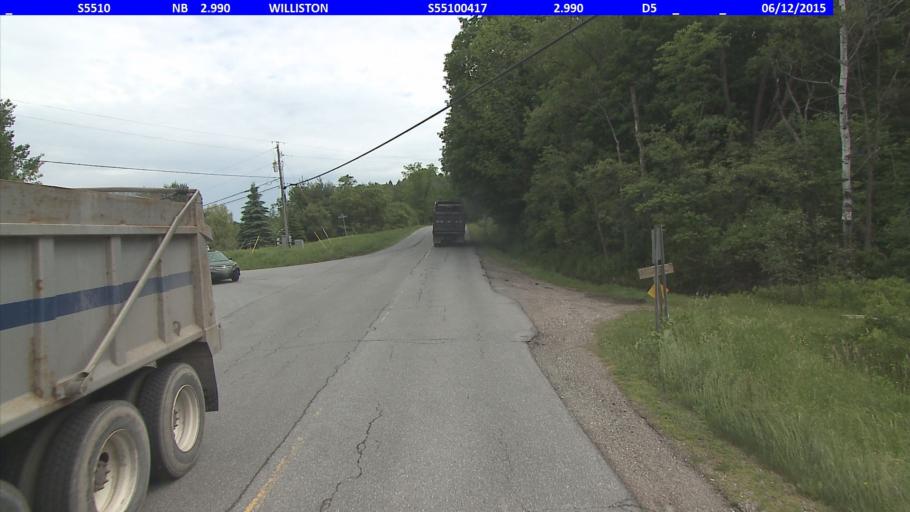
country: US
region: Vermont
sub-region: Chittenden County
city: Williston
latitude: 44.4146
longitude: -73.0870
